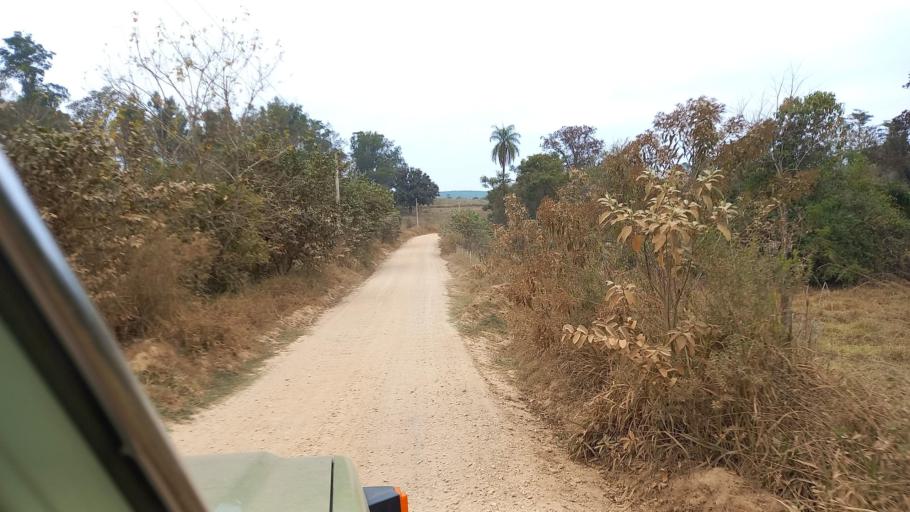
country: BR
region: Sao Paulo
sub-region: Moji-Guacu
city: Mogi-Gaucu
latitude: -22.3037
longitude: -46.8324
